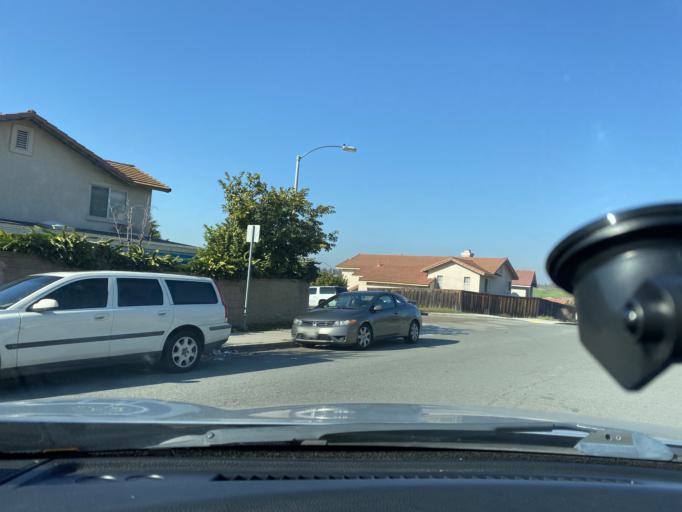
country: US
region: California
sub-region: San Diego County
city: National City
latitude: 32.7048
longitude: -117.0894
